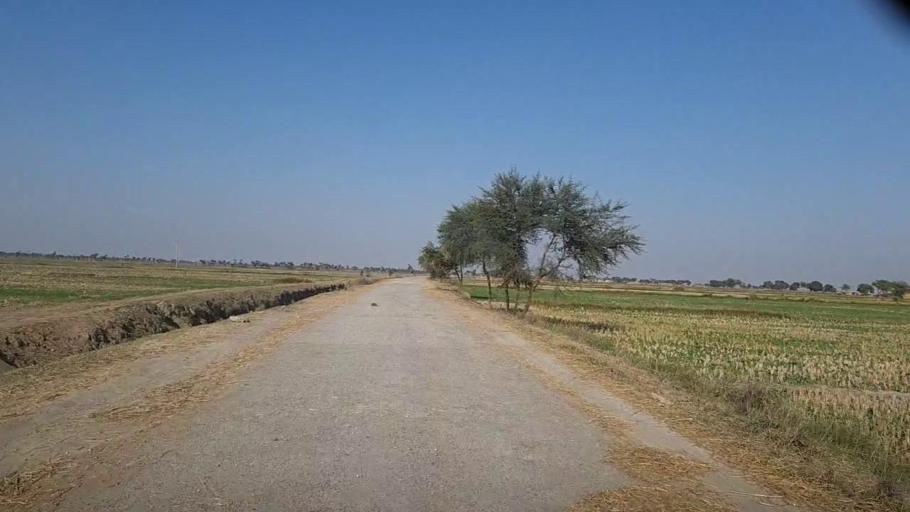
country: PK
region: Sindh
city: Thul
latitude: 28.3465
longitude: 68.7611
